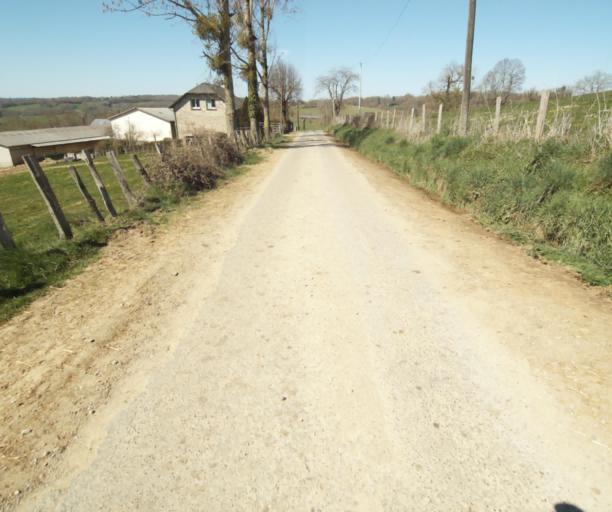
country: FR
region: Limousin
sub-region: Departement de la Correze
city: Chamboulive
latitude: 45.4467
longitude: 1.6764
